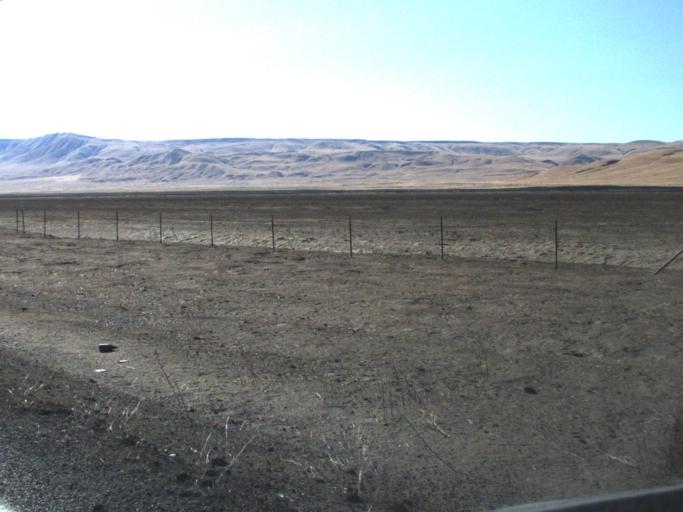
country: US
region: Washington
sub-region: Grant County
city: Desert Aire
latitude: 46.5545
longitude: -119.7006
